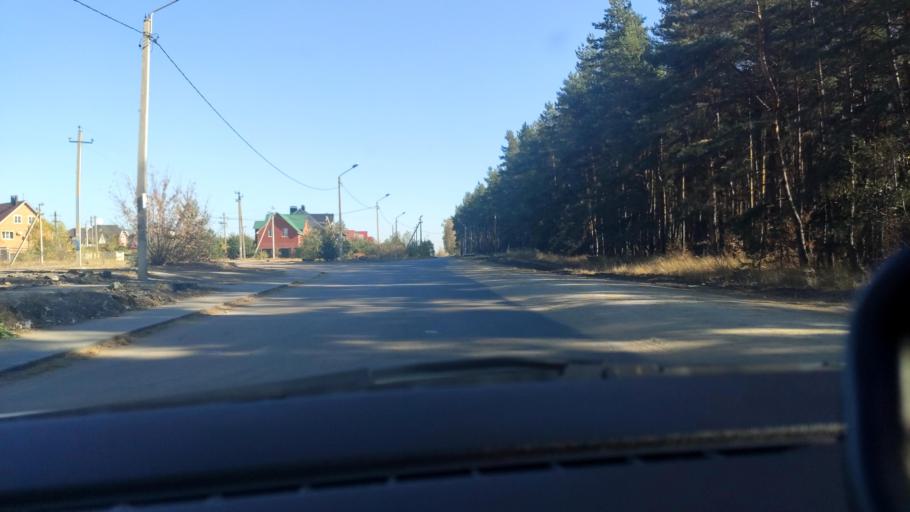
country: RU
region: Voronezj
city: Pridonskoy
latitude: 51.6261
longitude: 39.0868
